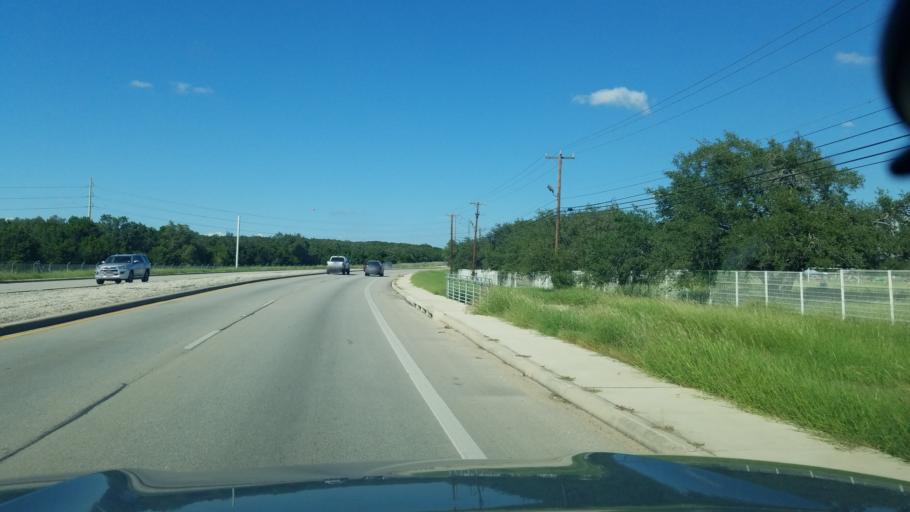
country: US
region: Texas
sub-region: Bexar County
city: Hollywood Park
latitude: 29.6393
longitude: -98.5200
